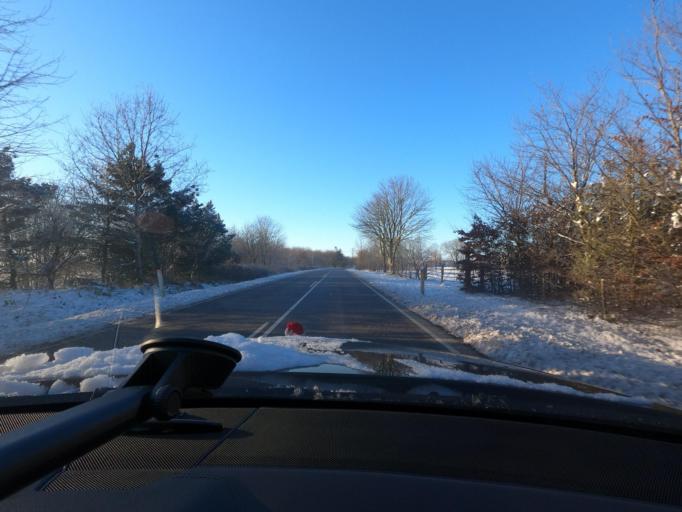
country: DK
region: South Denmark
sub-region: Aabenraa Kommune
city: Rodekro
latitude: 55.0751
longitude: 9.2525
